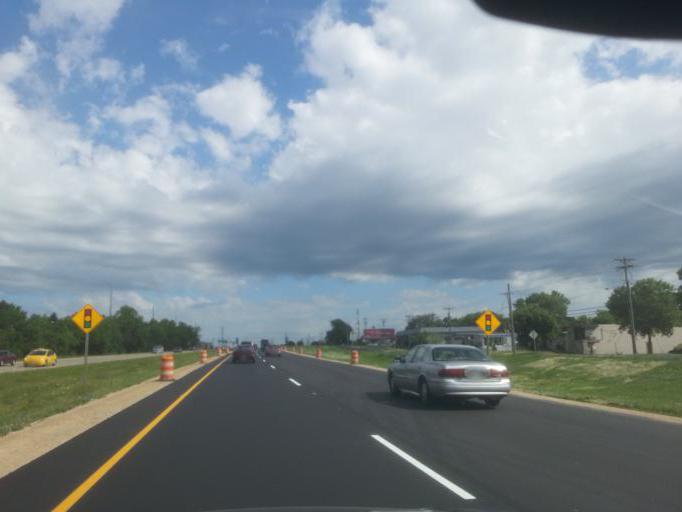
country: US
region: Wisconsin
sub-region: Dane County
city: Monona
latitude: 43.0580
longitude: -89.3092
